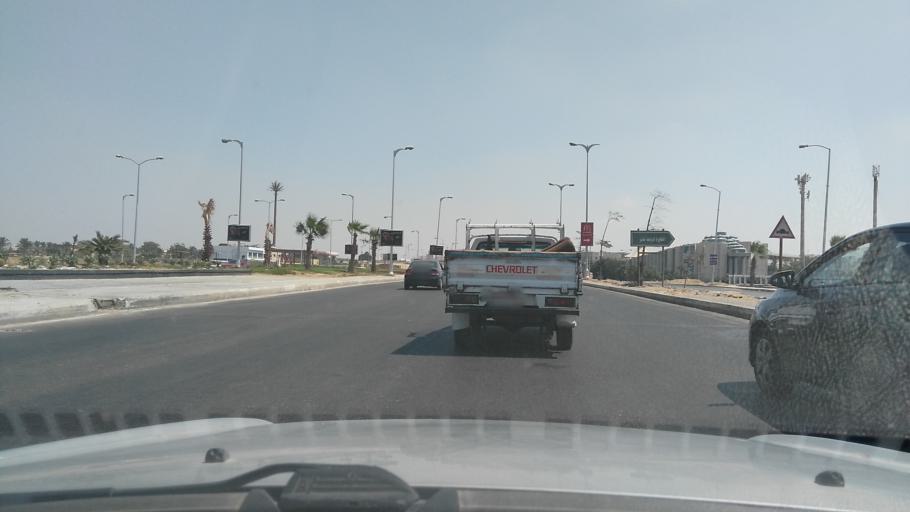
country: EG
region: Al Jizah
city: Madinat Sittah Uktubar
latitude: 29.9942
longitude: 30.9598
